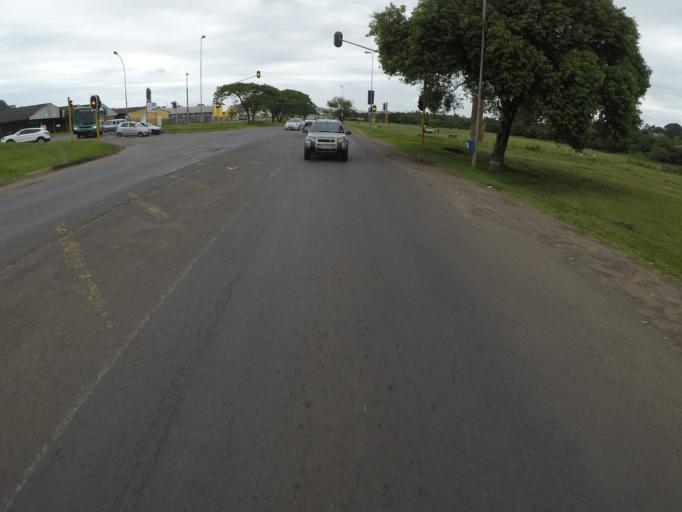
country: ZA
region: KwaZulu-Natal
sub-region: uThungulu District Municipality
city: Empangeni
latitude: -28.7683
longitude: 31.9043
